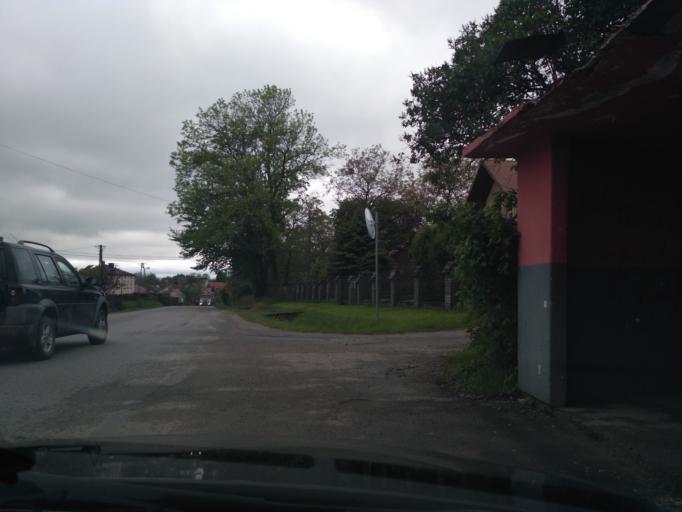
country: PL
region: Subcarpathian Voivodeship
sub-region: Powiat jasielski
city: Jaslo
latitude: 49.8028
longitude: 21.5155
